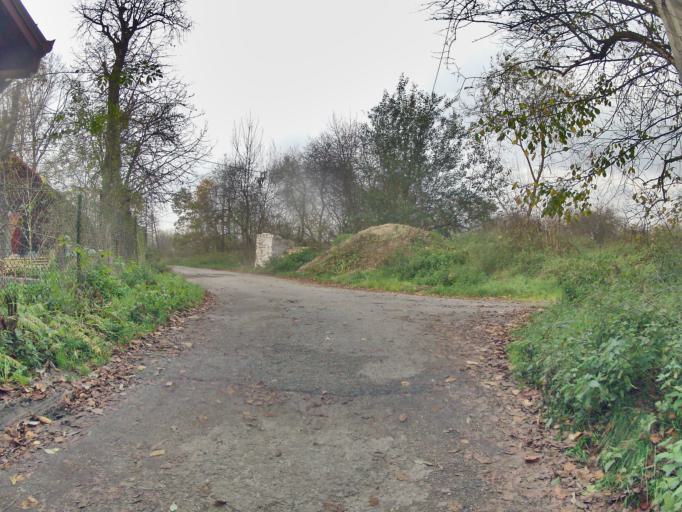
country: PL
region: Lesser Poland Voivodeship
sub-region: Powiat wielicki
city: Wegrzce Wielkie
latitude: 50.0455
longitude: 20.1057
